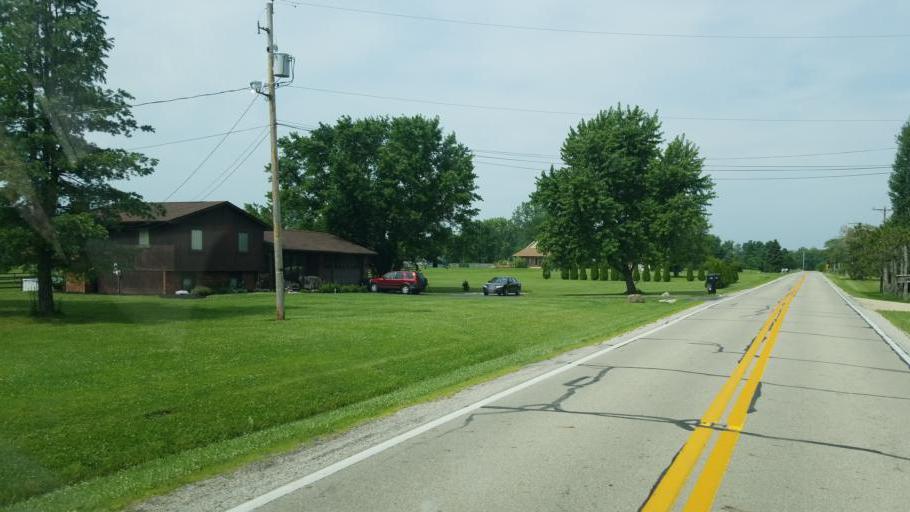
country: US
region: Ohio
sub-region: Madison County
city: West Jefferson
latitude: 39.8938
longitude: -83.2324
